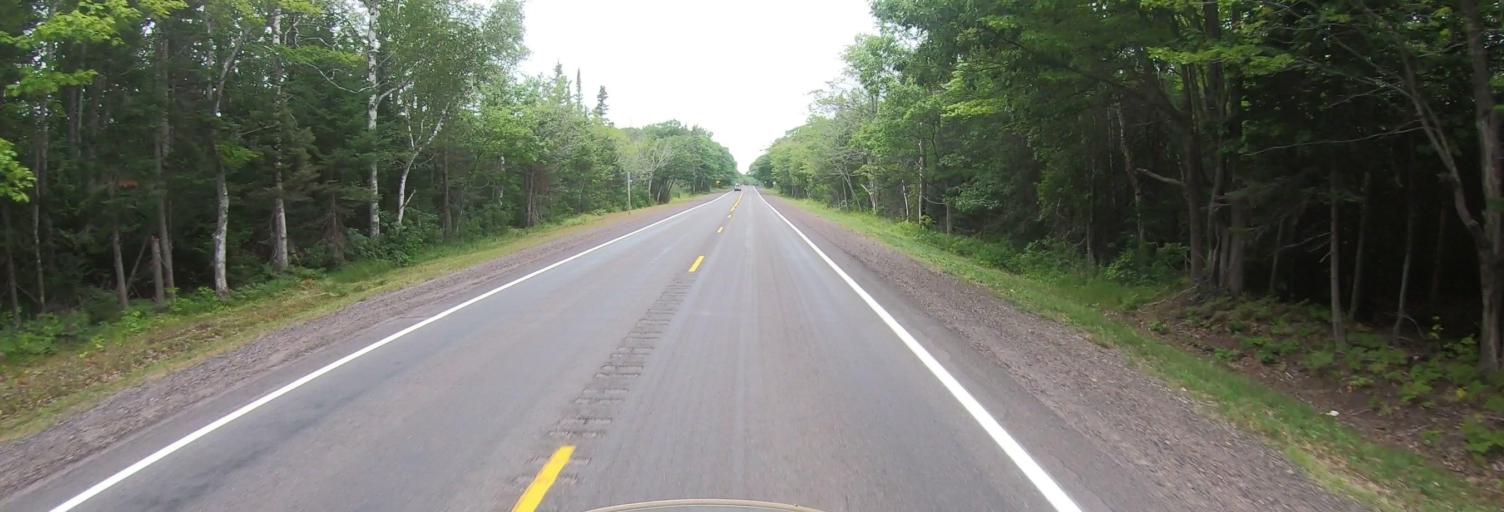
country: US
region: Michigan
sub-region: Keweenaw County
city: Eagle River
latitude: 47.3222
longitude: -88.3376
